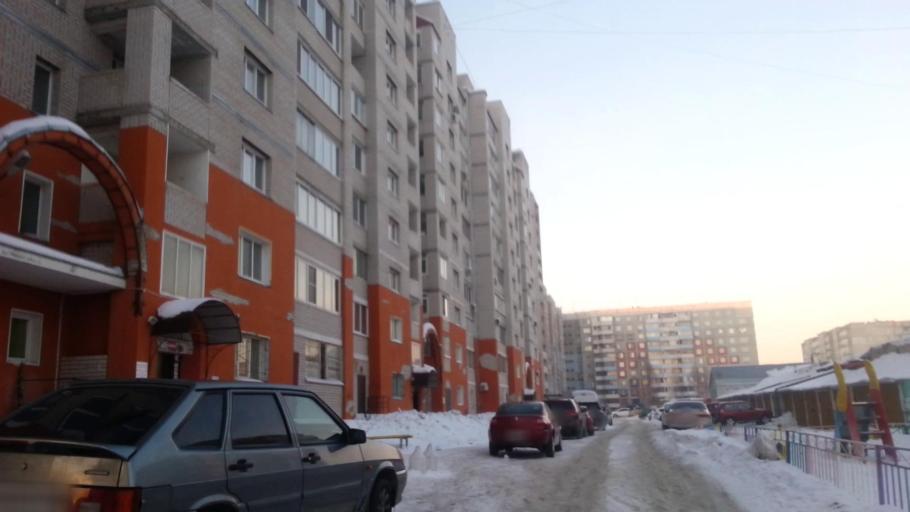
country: RU
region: Altai Krai
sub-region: Gorod Barnaulskiy
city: Barnaul
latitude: 53.3521
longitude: 83.6992
